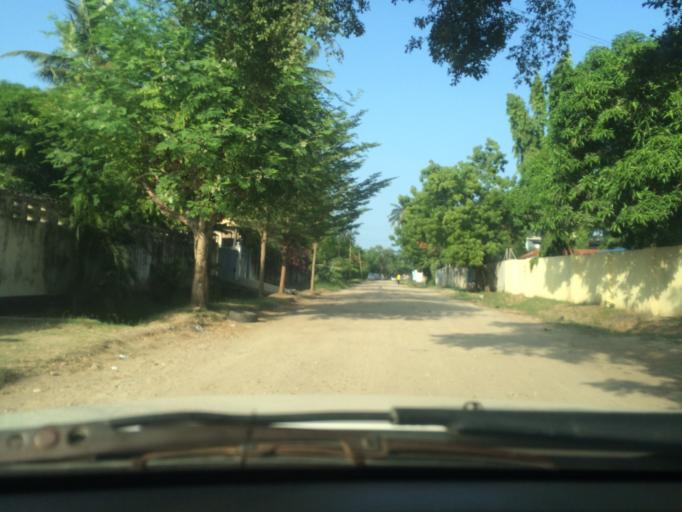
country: TZ
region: Dar es Salaam
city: Magomeni
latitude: -6.7751
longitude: 39.2554
